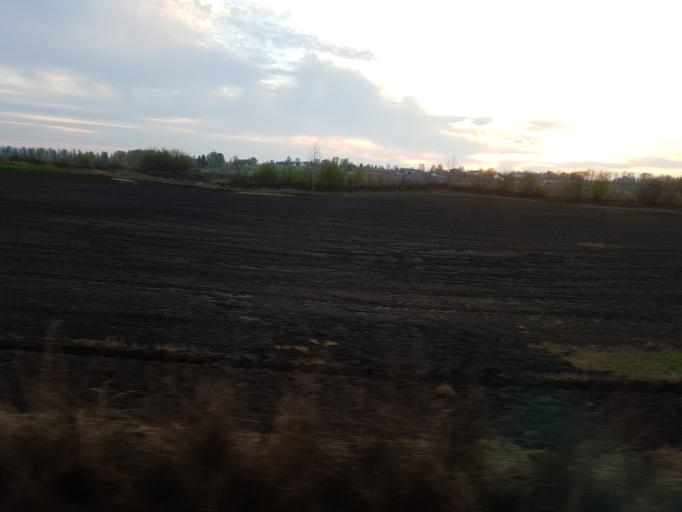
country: NO
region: Hedmark
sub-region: Hamar
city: Hamar
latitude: 60.7559
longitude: 11.1122
